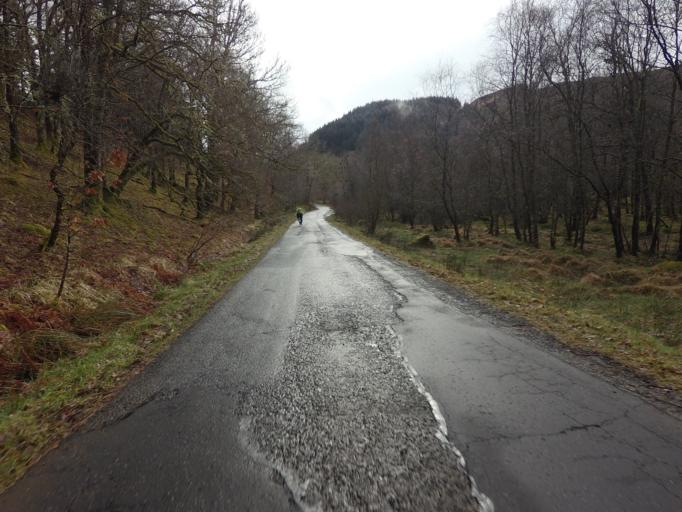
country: GB
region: Scotland
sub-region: West Dunbartonshire
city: Balloch
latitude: 56.2075
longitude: -4.5336
